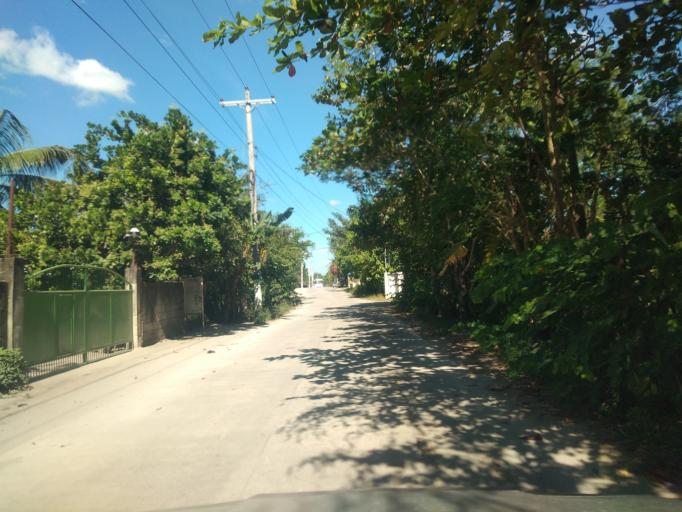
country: PH
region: Central Luzon
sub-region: Province of Pampanga
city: Bacolor
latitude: 15.0052
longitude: 120.6423
